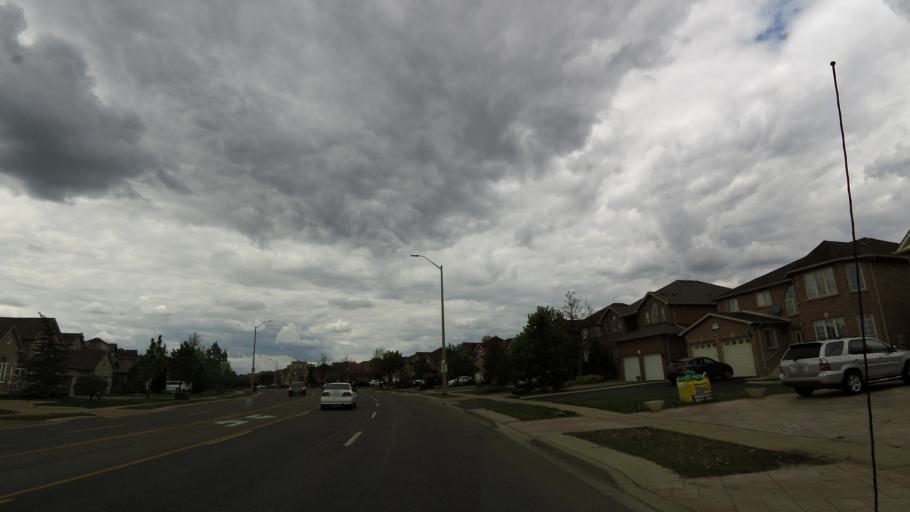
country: CA
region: Ontario
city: Mississauga
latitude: 43.5739
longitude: -79.6768
